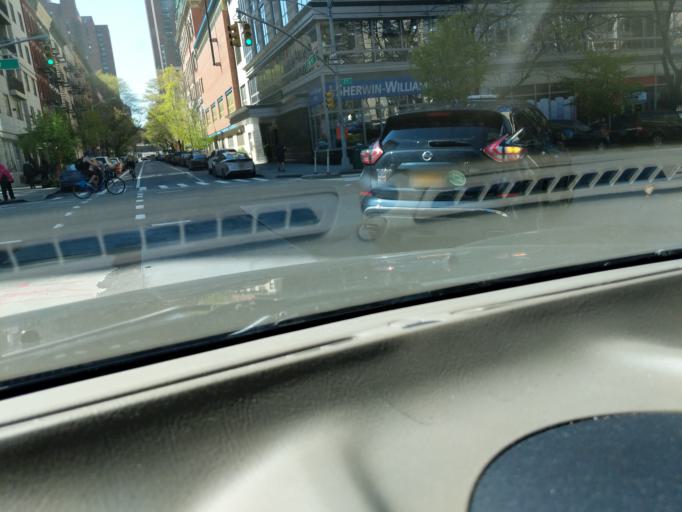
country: US
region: New York
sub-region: New York County
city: Manhattan
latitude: 40.7800
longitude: -73.9470
